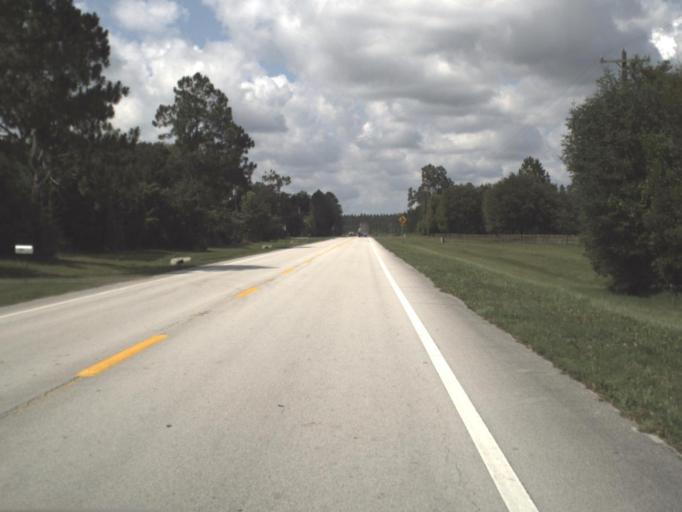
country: US
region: Florida
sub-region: Baker County
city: Macclenny
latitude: 30.2232
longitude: -82.1482
